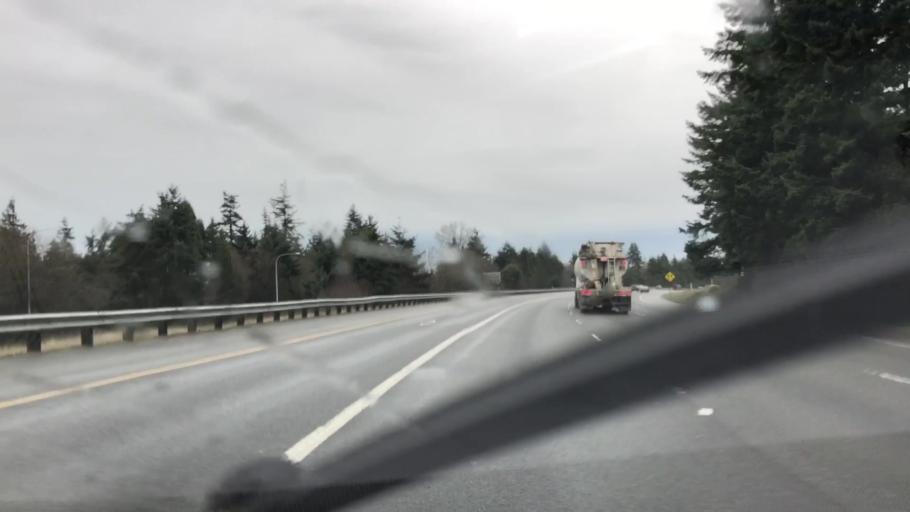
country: US
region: Washington
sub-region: Snohomish County
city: Mountlake Terrace
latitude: 47.8009
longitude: -122.3134
